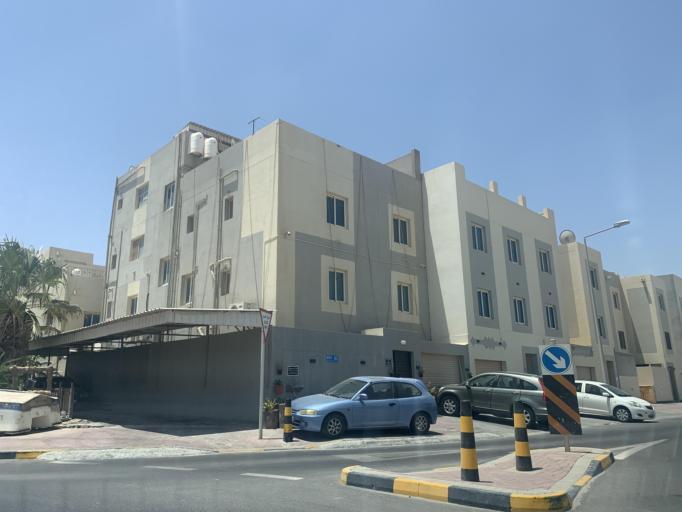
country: BH
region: Manama
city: Jidd Hafs
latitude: 26.2361
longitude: 50.4675
